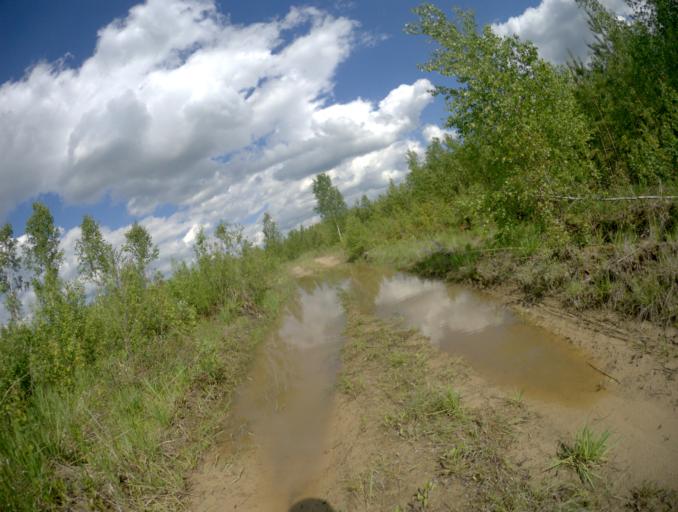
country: RU
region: Vladimir
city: Velikodvorskiy
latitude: 55.2779
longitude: 40.8804
